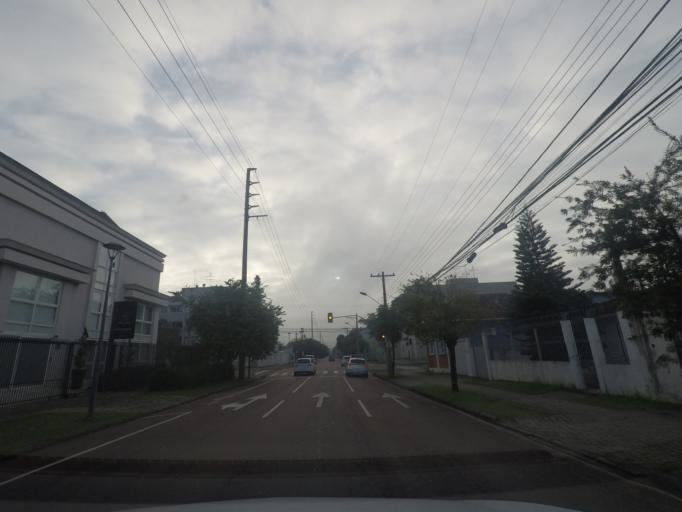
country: BR
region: Parana
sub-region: Curitiba
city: Curitiba
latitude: -25.4447
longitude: -49.2629
